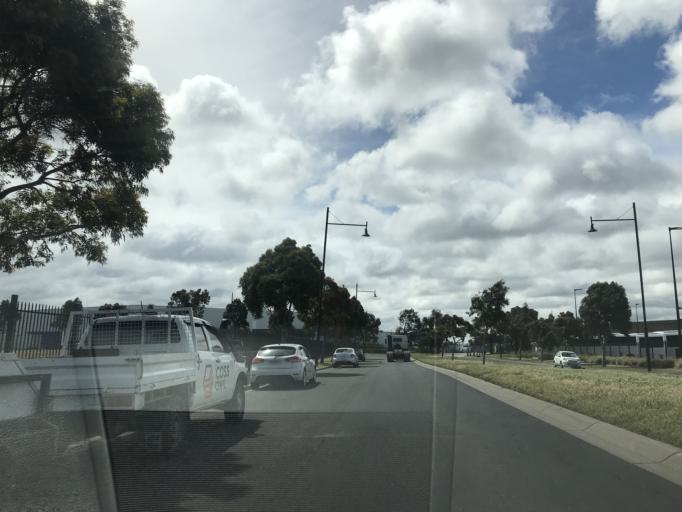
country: AU
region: Victoria
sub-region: Wyndham
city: Truganina
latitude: -37.8098
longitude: 144.7661
